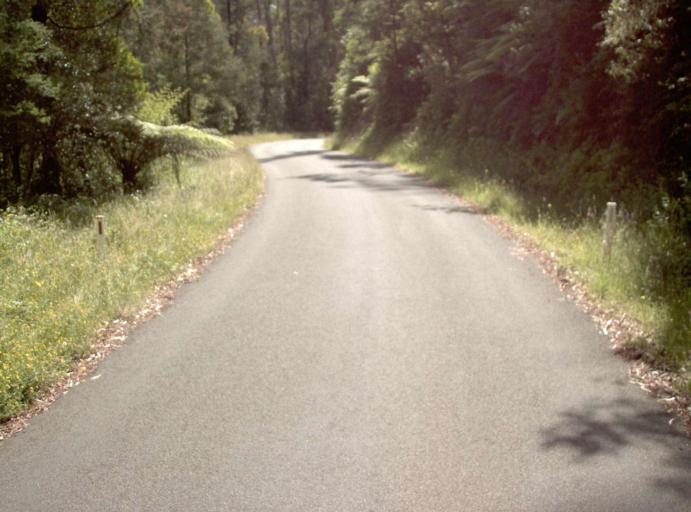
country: AU
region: Victoria
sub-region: Latrobe
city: Moe
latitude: -37.8485
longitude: 146.2221
